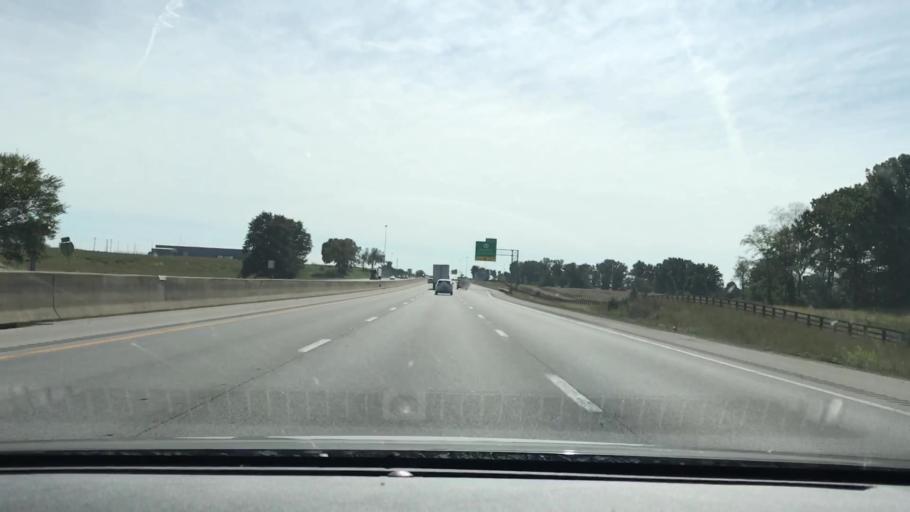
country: US
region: Kentucky
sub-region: Simpson County
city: Franklin
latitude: 36.7254
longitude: -86.5171
